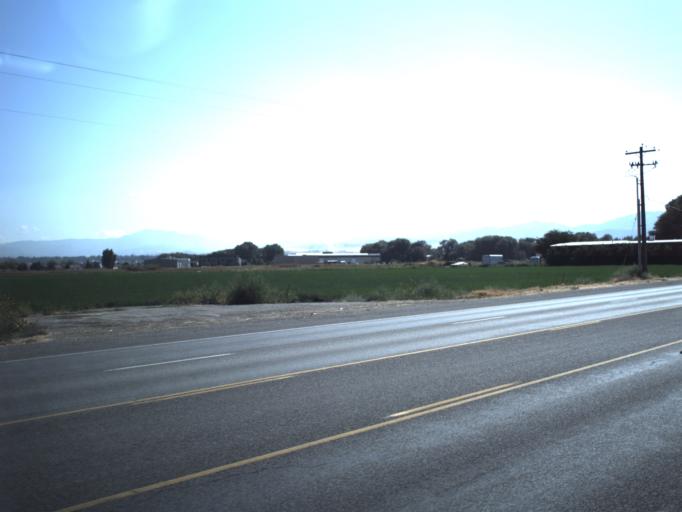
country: US
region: Utah
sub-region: Cache County
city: Nibley
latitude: 41.6841
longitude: -111.8745
